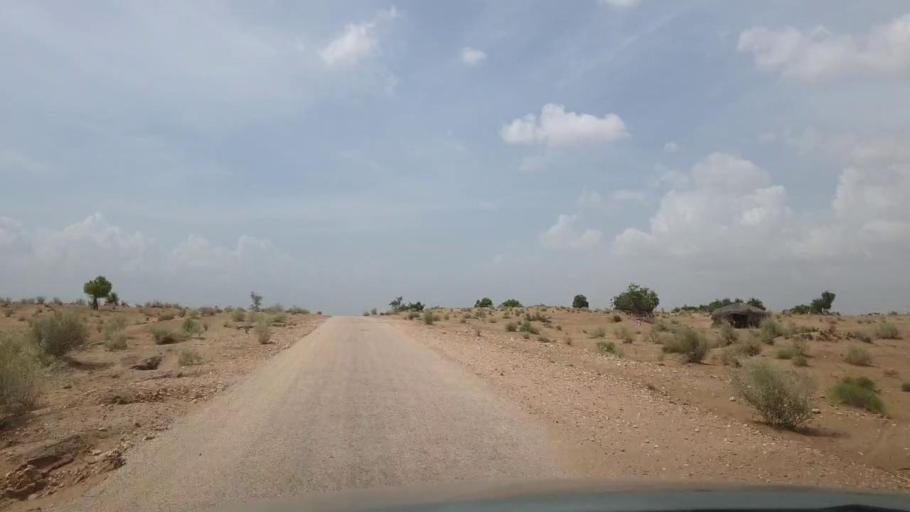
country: PK
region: Sindh
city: Kot Diji
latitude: 27.2067
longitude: 69.0848
